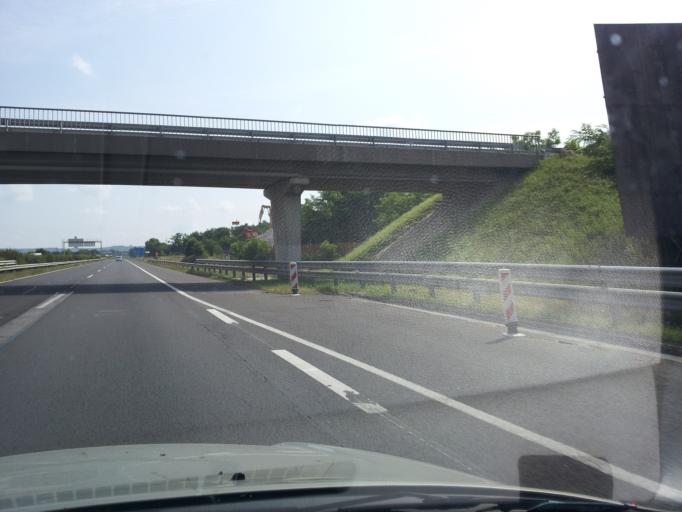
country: HU
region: Pest
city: Fot
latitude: 47.5796
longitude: 19.1676
